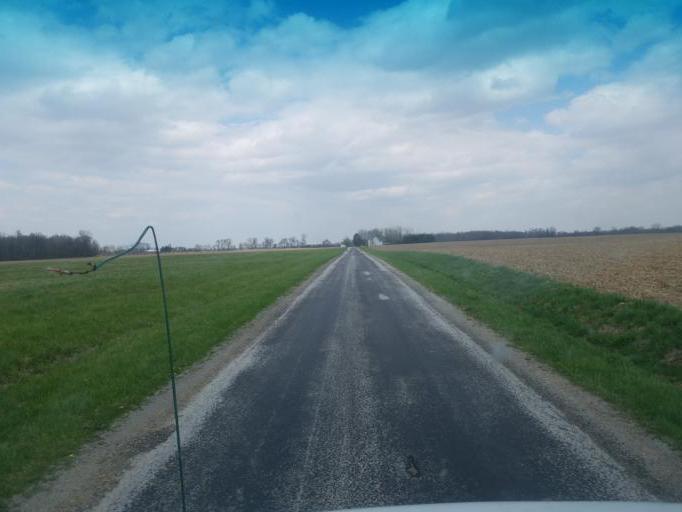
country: US
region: Ohio
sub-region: Wyandot County
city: Upper Sandusky
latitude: 40.9363
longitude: -83.2381
